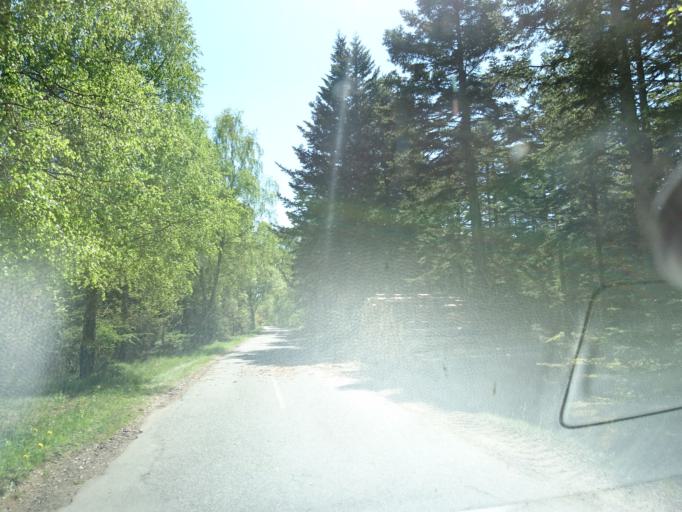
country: DK
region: North Denmark
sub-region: Hjorring Kommune
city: Sindal
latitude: 57.5939
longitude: 10.2294
